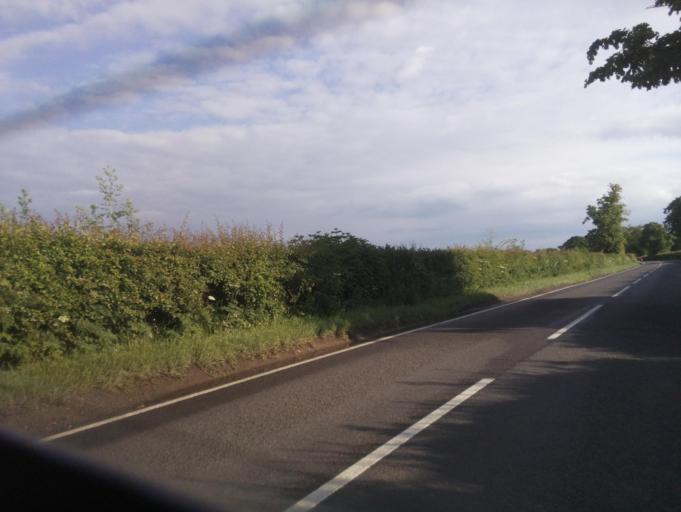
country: GB
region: England
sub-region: Lincolnshire
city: Navenby
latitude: 53.0646
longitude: -0.6367
